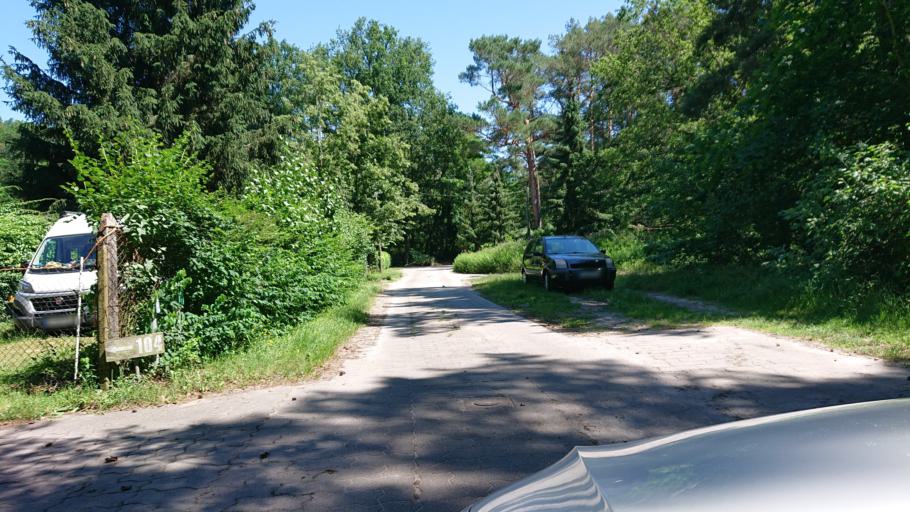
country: DE
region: Brandenburg
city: Potsdam
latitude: 52.3477
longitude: 13.1207
